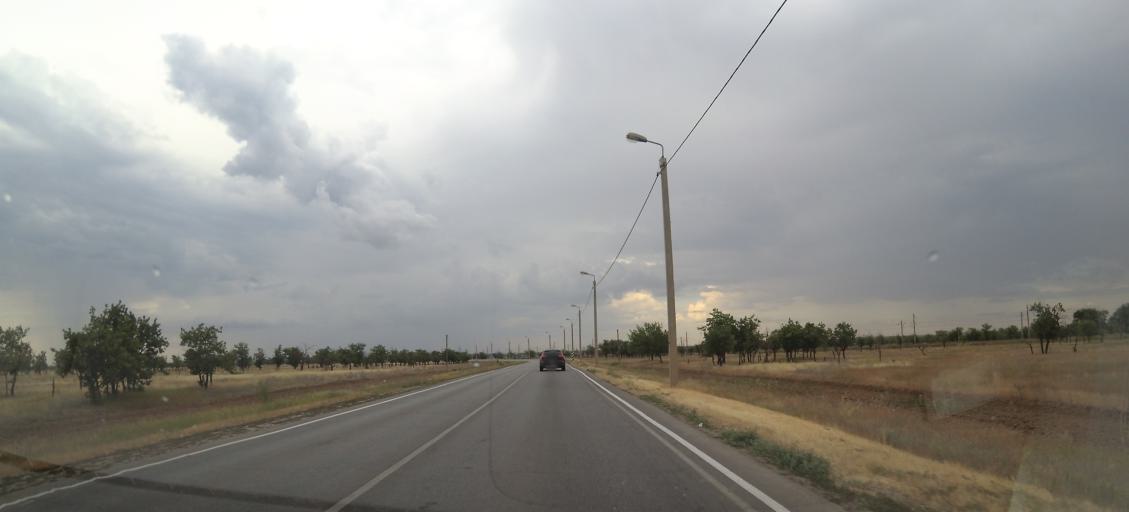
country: RU
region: Volgograd
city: Kotel'nikovo
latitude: 47.6133
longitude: 43.1226
